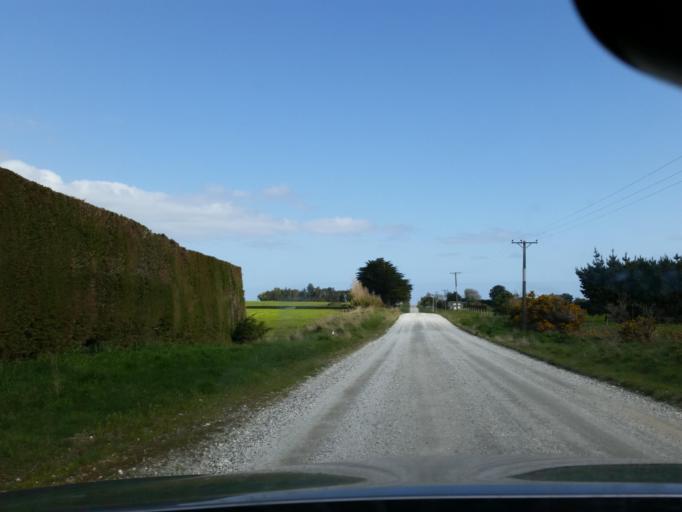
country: NZ
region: Southland
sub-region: Invercargill City
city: Invercargill
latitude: -46.4112
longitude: 168.5061
